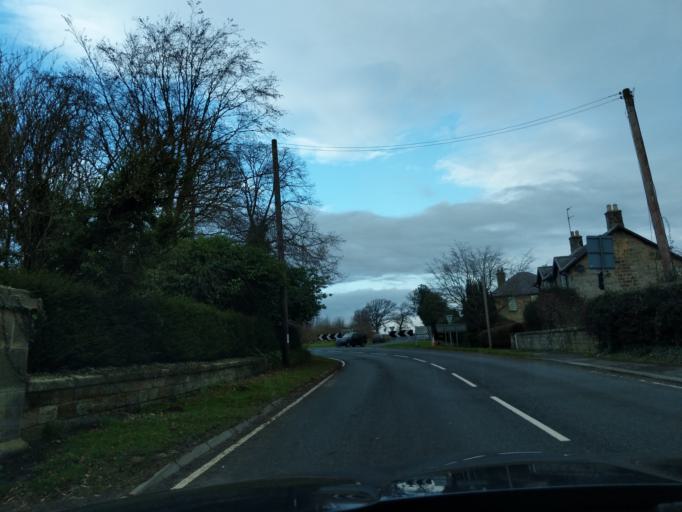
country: GB
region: England
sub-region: Northumberland
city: Meldon
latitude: 55.1052
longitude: -1.8436
